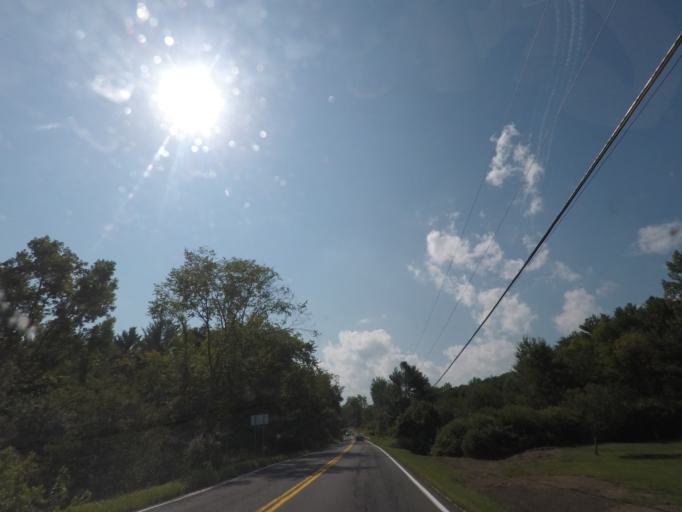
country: US
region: New York
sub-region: Rensselaer County
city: Hoosick Falls
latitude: 42.8240
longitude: -73.4855
